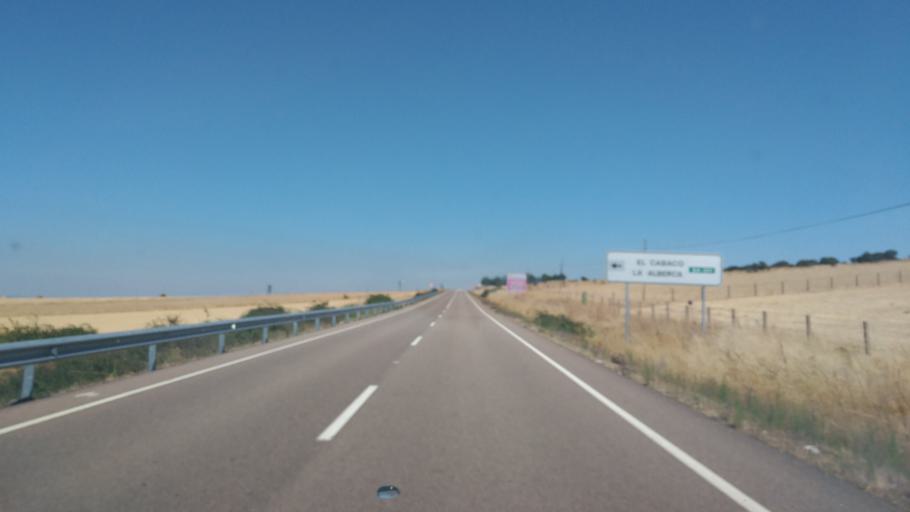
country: ES
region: Castille and Leon
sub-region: Provincia de Salamanca
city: Tamames
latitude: 40.6519
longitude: -6.1164
